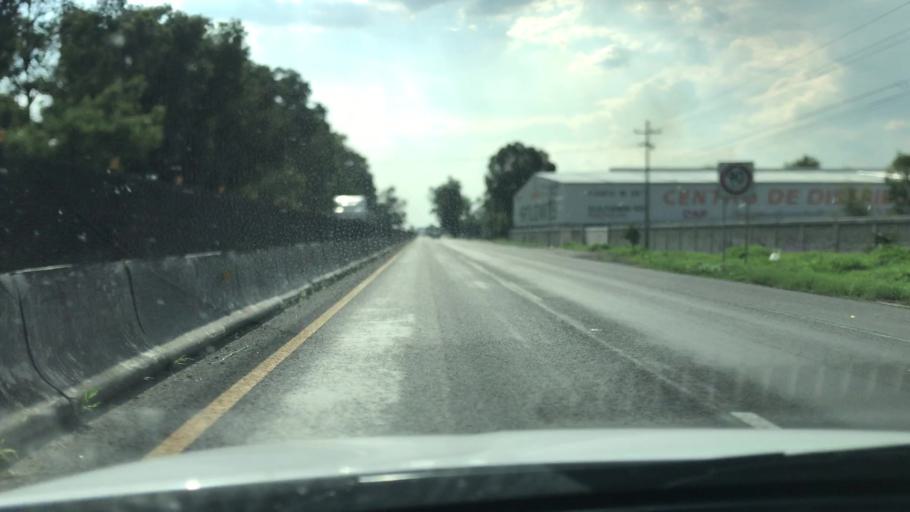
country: MX
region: Guanajuato
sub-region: Salamanca
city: El Divisador
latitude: 20.5542
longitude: -101.1537
